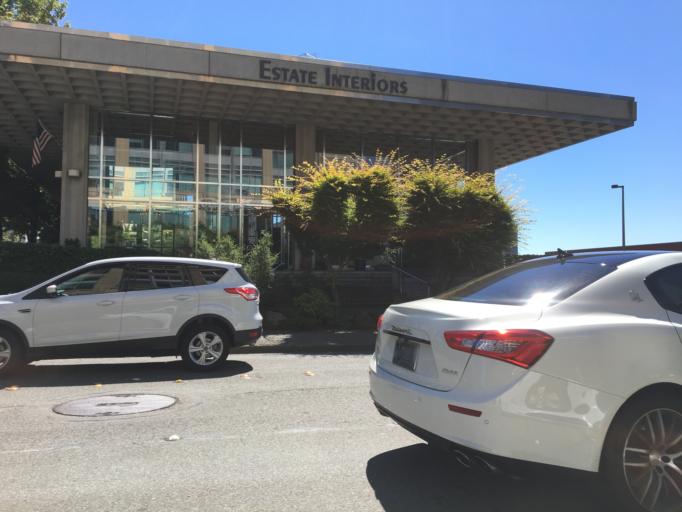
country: US
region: Washington
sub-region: King County
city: Bellevue
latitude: 47.6123
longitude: -122.1958
